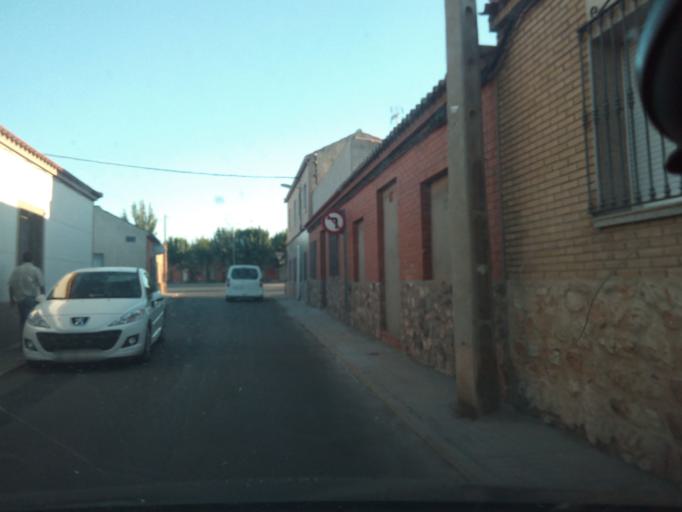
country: ES
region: Castille-La Mancha
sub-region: Province of Toledo
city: Villacanas
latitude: 39.6180
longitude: -3.3392
